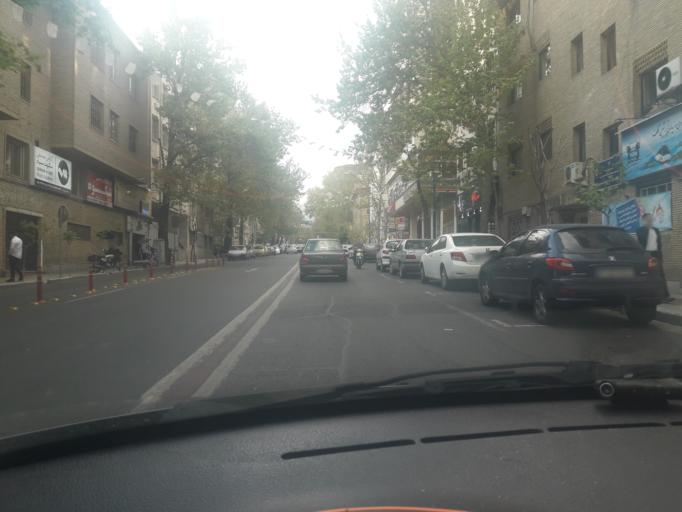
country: IR
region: Tehran
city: Tehran
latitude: 35.7426
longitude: 51.4051
